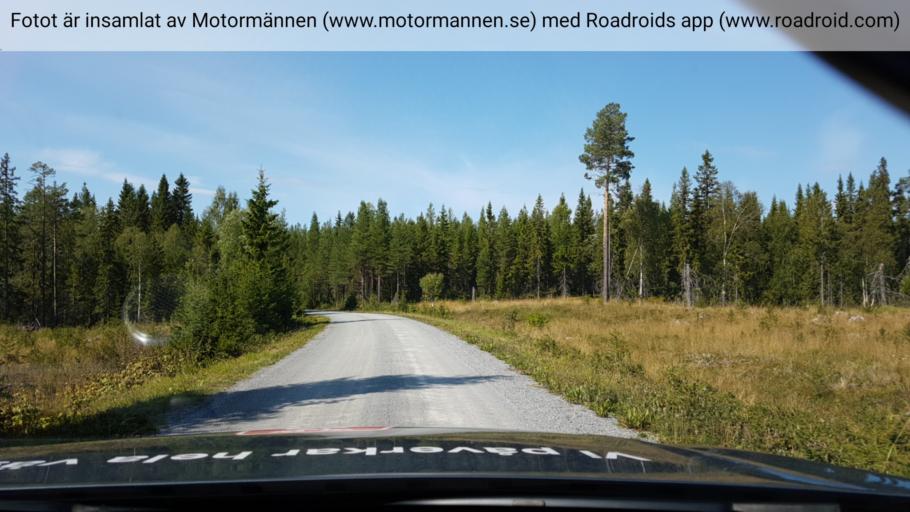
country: SE
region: Jaemtland
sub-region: OEstersunds Kommun
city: Ostersund
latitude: 63.1138
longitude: 14.5196
